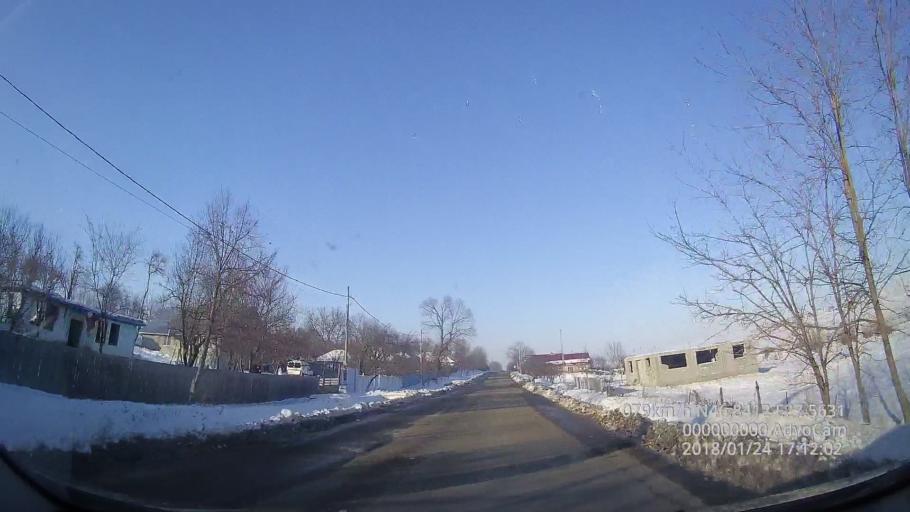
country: RO
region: Vaslui
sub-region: Comuna Rebricea
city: Rebricea
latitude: 46.8420
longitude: 27.5630
